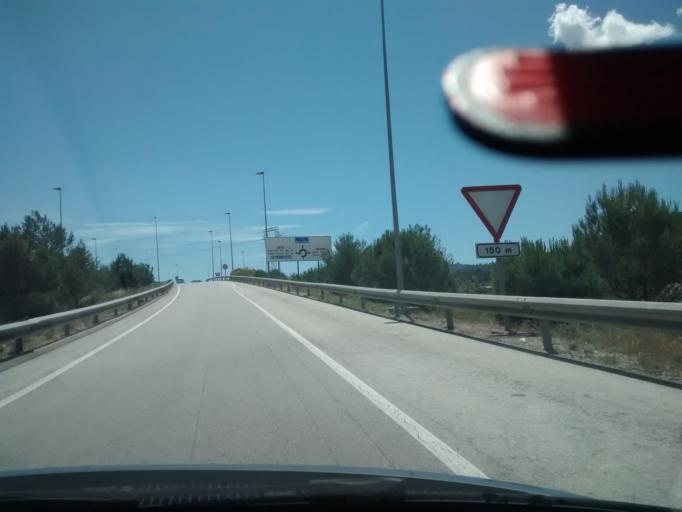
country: ES
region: Catalonia
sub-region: Provincia de Barcelona
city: Sant Vicenc dels Horts
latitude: 41.3911
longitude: 2.0181
